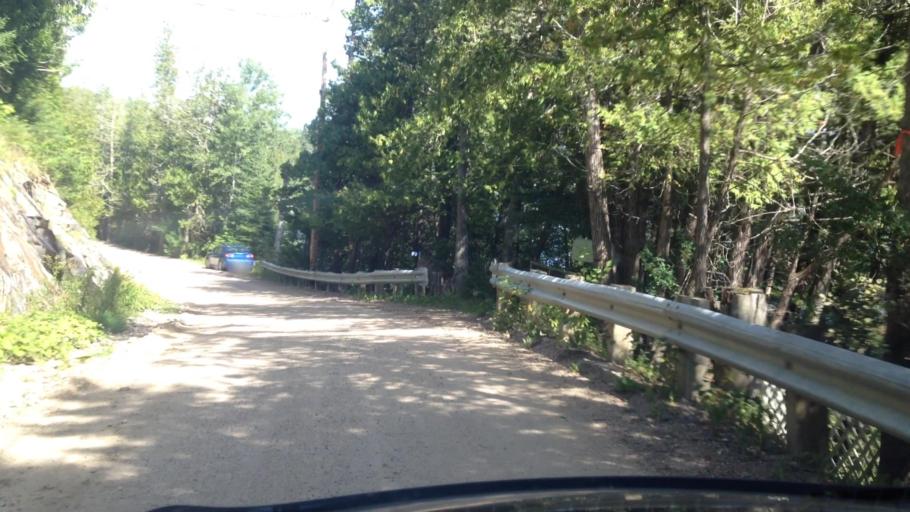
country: CA
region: Quebec
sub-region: Laurentides
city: Mont-Tremblant
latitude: 45.9373
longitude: -74.5844
